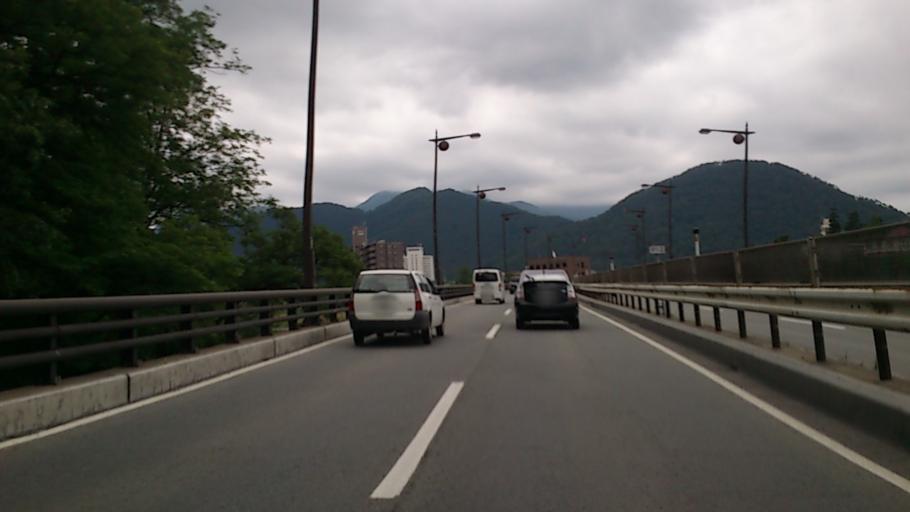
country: JP
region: Yamagata
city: Yamagata-shi
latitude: 38.2509
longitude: 140.3557
